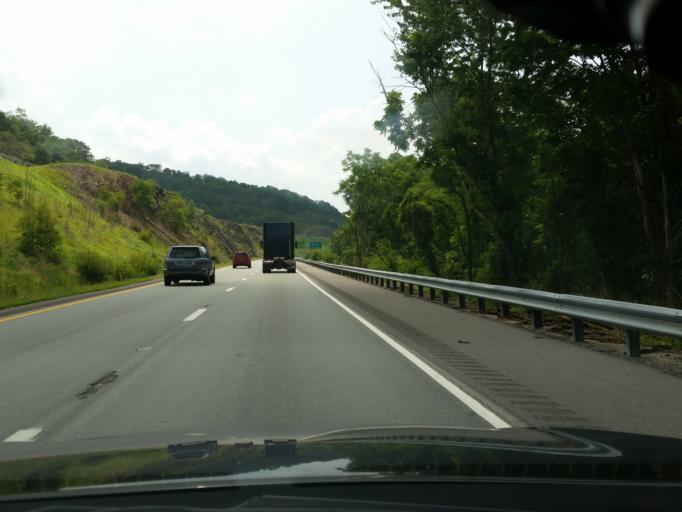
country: US
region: Pennsylvania
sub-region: Perry County
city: Duncannon
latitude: 40.4608
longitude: -77.0272
